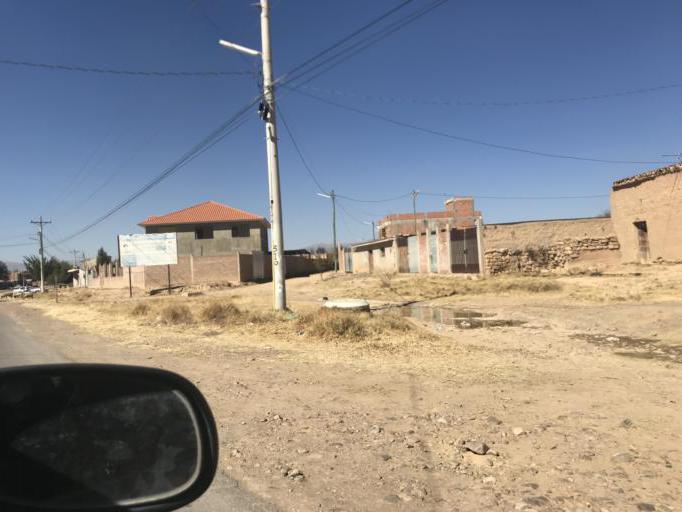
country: BO
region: Cochabamba
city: Cliza
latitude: -17.5983
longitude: -65.9590
